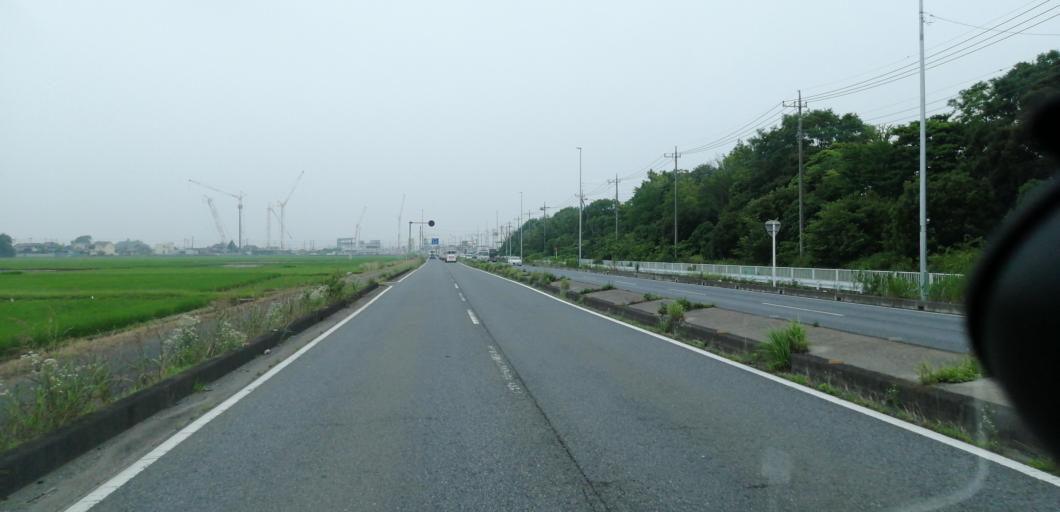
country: JP
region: Saitama
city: Hanyu
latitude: 36.1499
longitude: 139.5353
